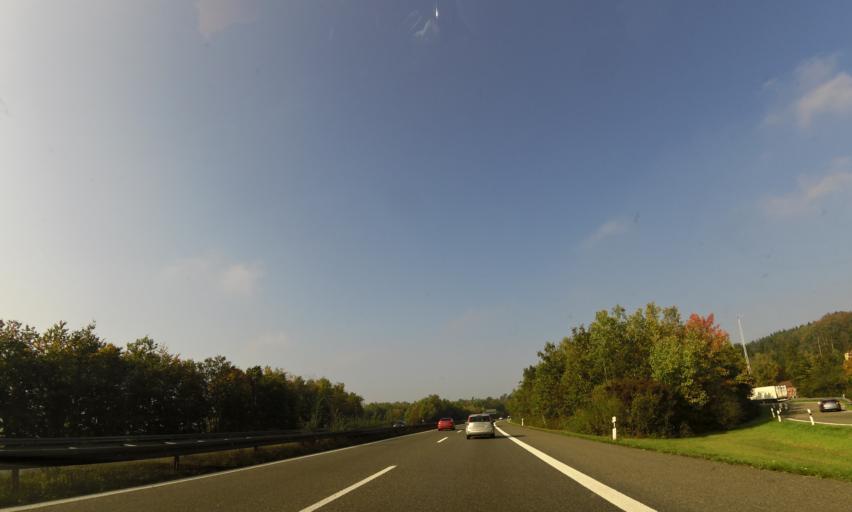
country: DE
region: Bavaria
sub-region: Regierungsbezirk Mittelfranken
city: Schnelldorf
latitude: 49.2052
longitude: 10.2030
